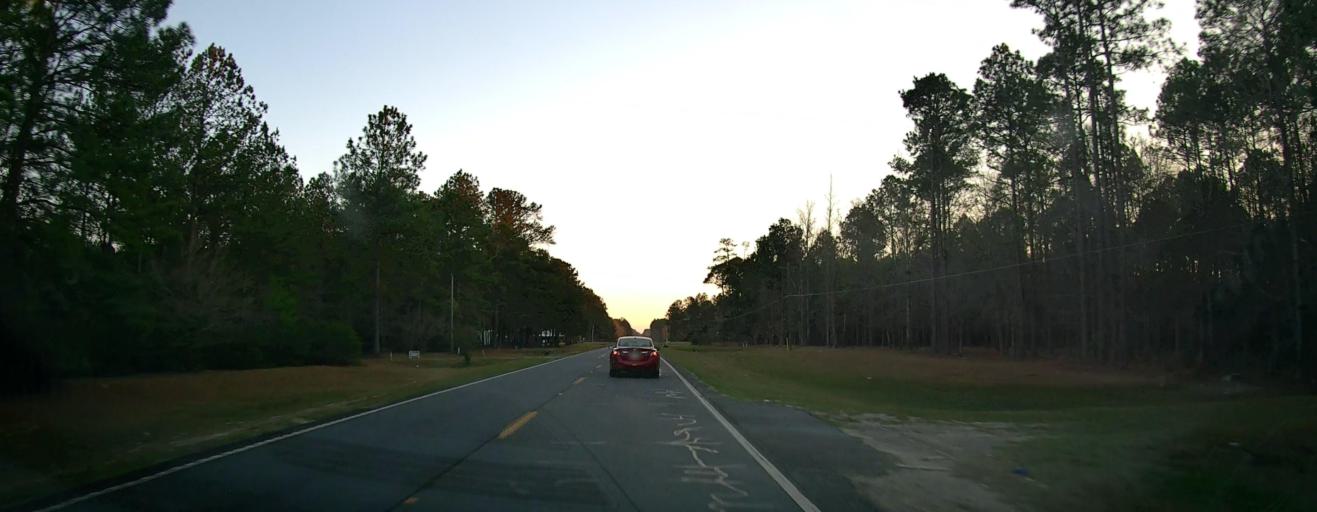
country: US
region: Georgia
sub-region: Dodge County
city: Eastman
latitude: 32.2429
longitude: -83.1459
